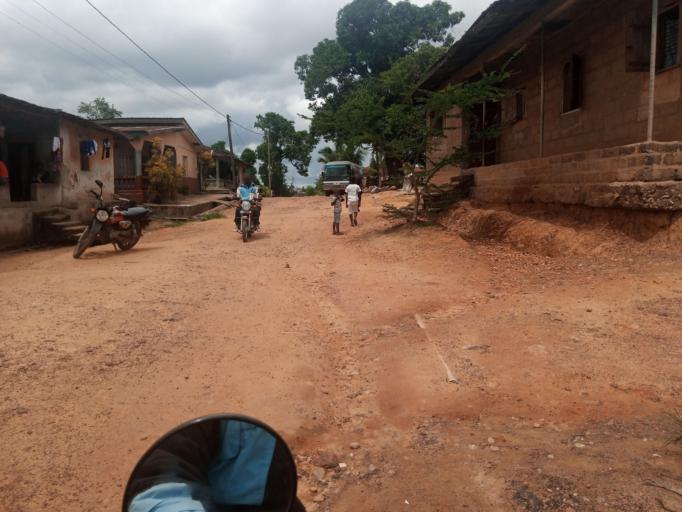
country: SL
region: Southern Province
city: Bo
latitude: 7.9550
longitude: -11.7406
